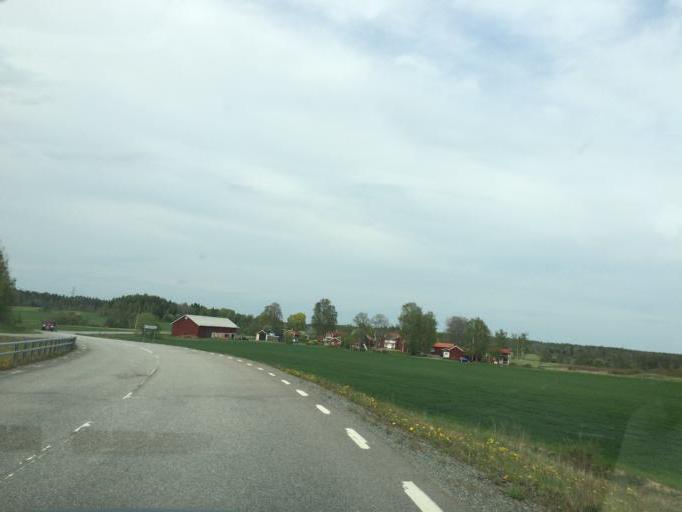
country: SE
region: Vaestmanland
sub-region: Kopings Kommun
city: Koping
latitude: 59.5356
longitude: 15.9545
